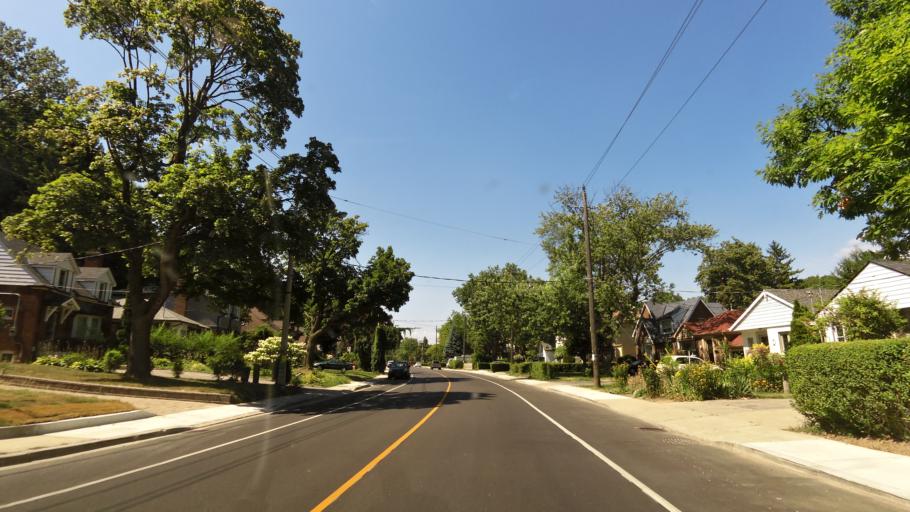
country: CA
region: Ontario
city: Toronto
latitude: 43.6394
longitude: -79.4770
